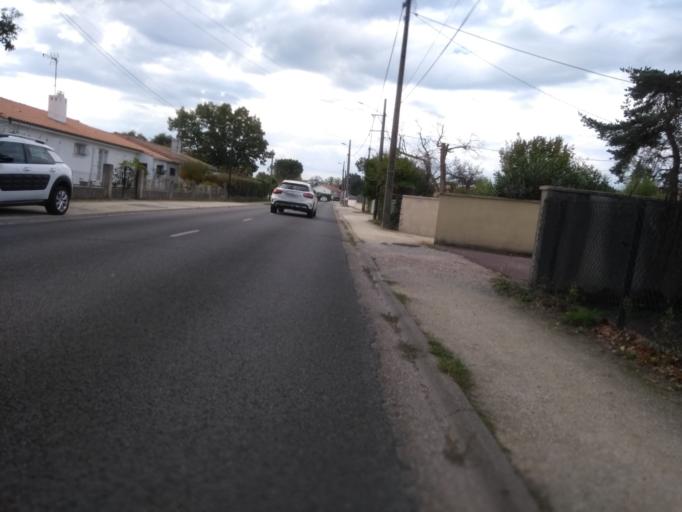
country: FR
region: Aquitaine
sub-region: Departement de la Gironde
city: Cestas
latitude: 44.7787
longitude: -0.6917
